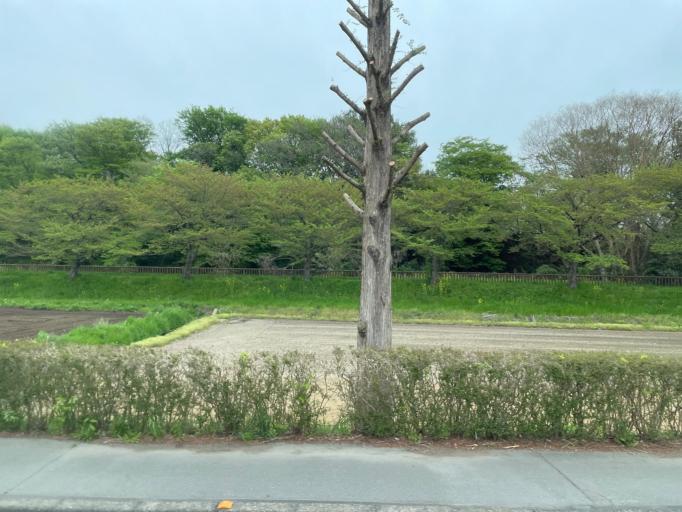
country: JP
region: Saitama
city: Saitama
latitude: 35.8963
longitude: 139.7029
